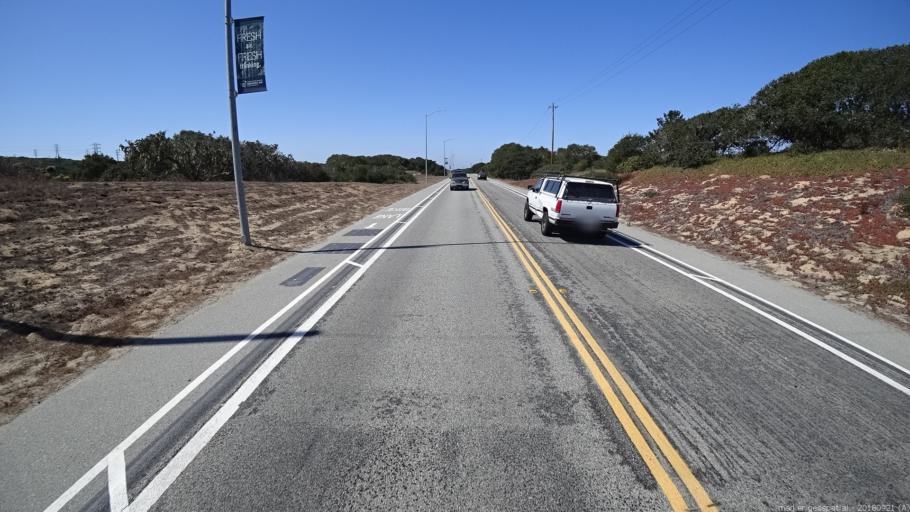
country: US
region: California
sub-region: Monterey County
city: Marina
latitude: 36.6551
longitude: -121.7685
